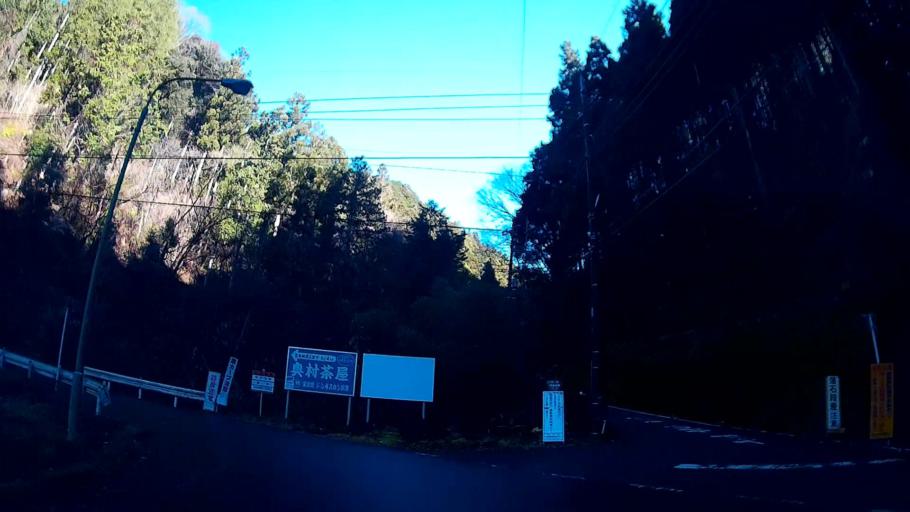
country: JP
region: Saitama
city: Chichibu
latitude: 35.9506
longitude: 139.1779
